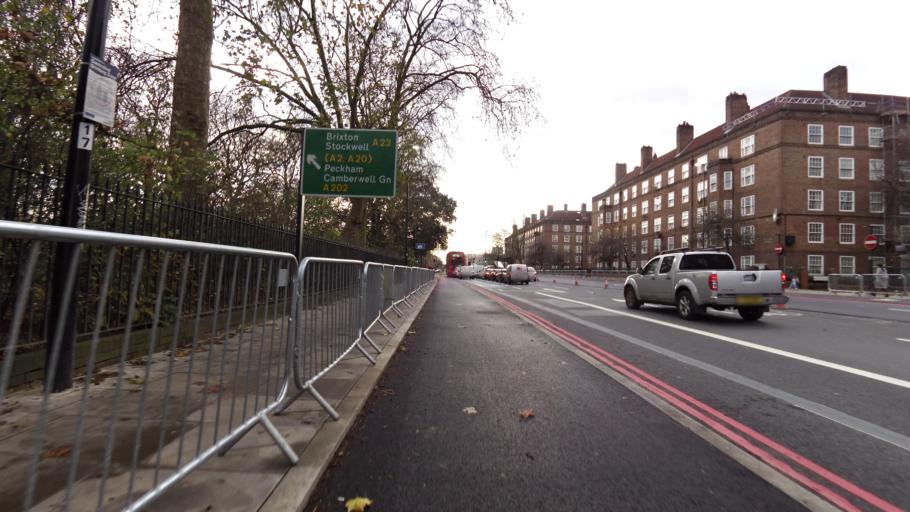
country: GB
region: England
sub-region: Greater London
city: Kennington
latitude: 51.4836
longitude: -0.1106
